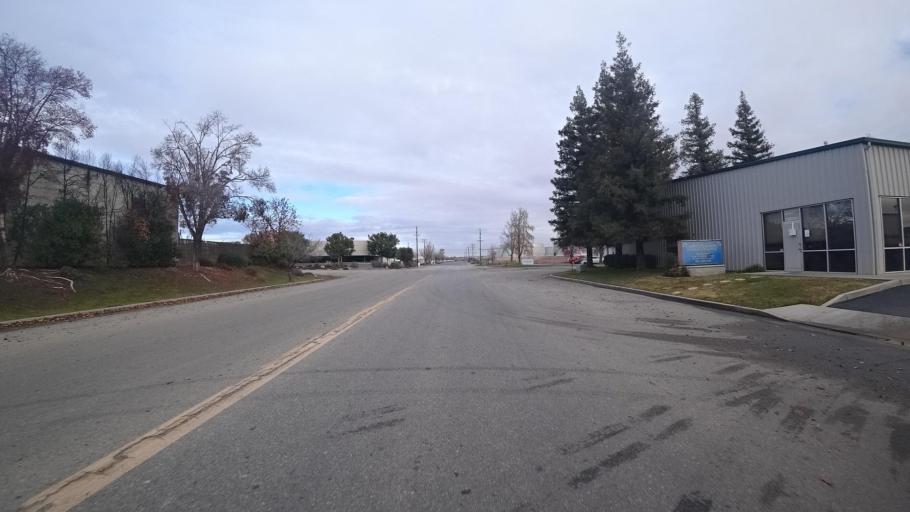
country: US
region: California
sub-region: Kern County
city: Bakersfield
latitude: 35.3893
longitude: -119.0590
